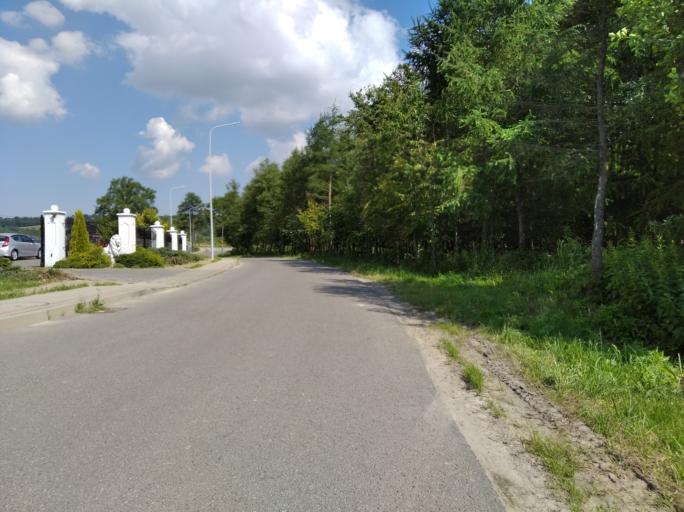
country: PL
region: Subcarpathian Voivodeship
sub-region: Powiat rzeszowski
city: Dynow
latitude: 49.8329
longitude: 22.2242
